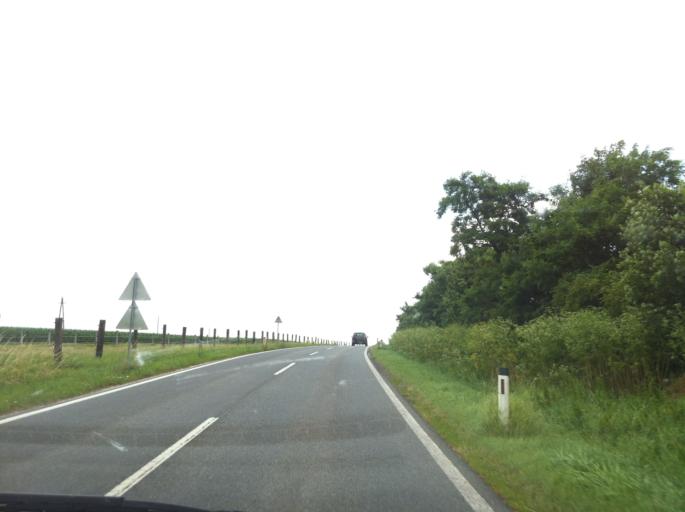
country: AT
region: Lower Austria
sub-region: Politischer Bezirk Tulln
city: Tulbing
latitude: 48.2723
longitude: 16.0695
